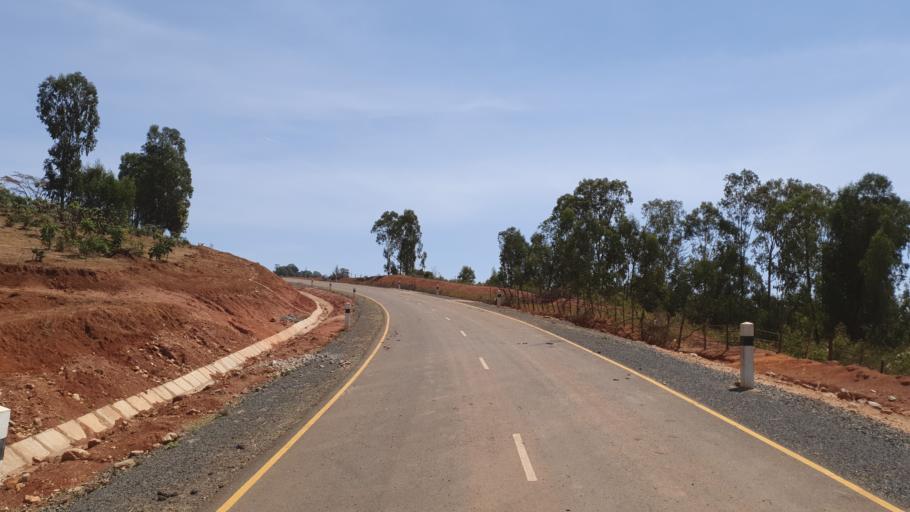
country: ET
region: Oromiya
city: Shambu
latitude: 9.8861
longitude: 36.6521
